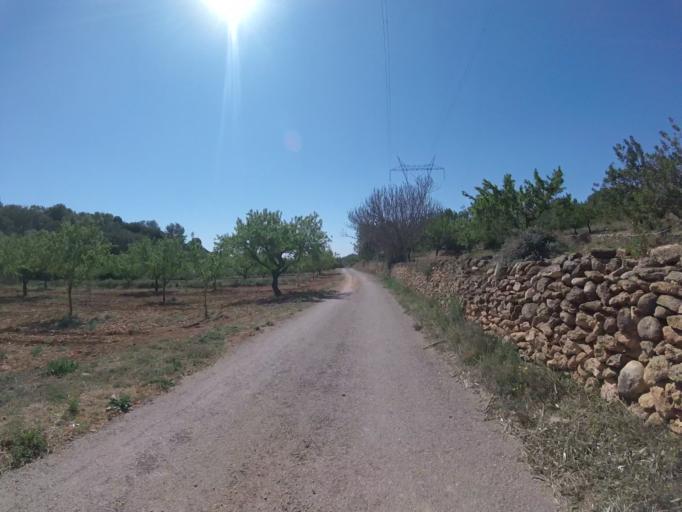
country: ES
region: Valencia
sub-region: Provincia de Castello
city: Cuevas de Vinroma
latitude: 40.3721
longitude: 0.1346
